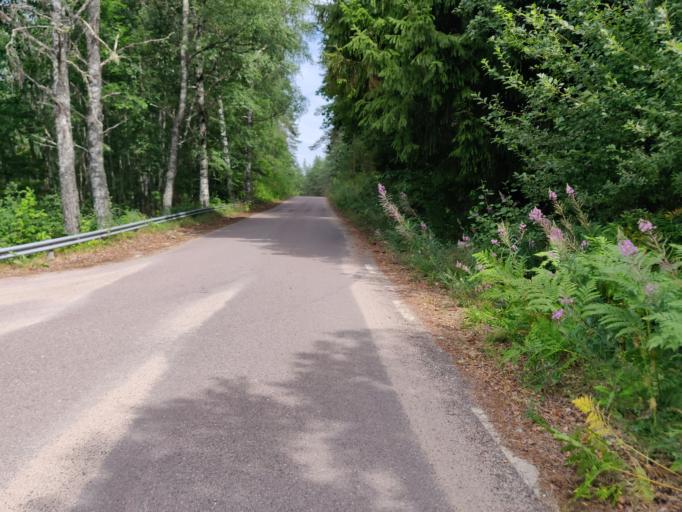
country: SE
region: Vaermland
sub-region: Munkfors Kommun
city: Munkfors
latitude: 59.9587
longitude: 13.5292
